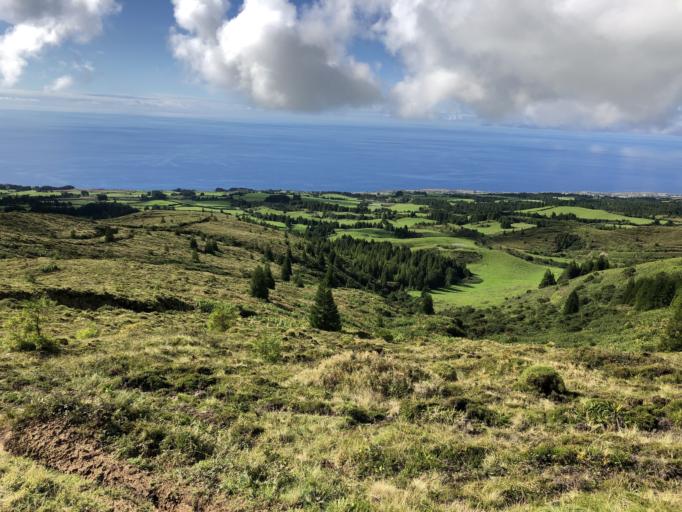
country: PT
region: Azores
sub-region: Ponta Delgada
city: Arrifes
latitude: 37.8291
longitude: -25.7575
